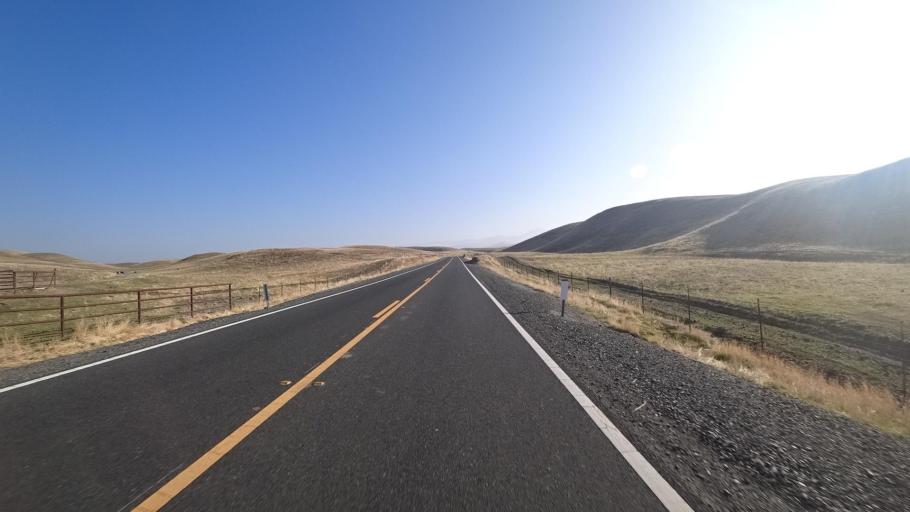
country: US
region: California
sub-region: Tulare County
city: Richgrove
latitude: 35.7427
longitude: -118.9477
